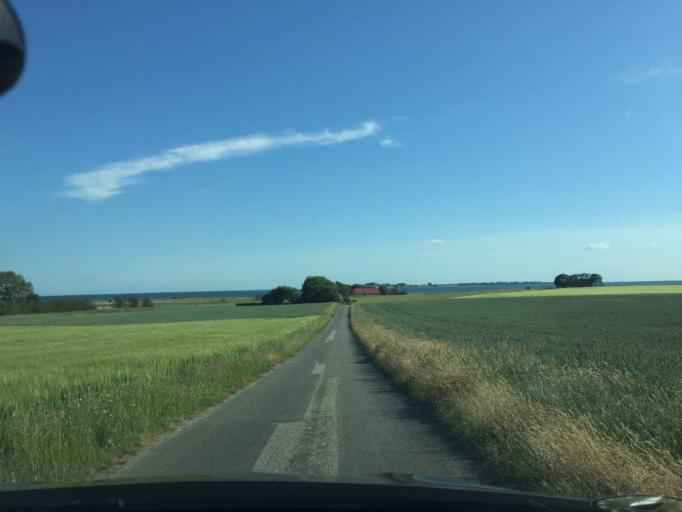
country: DK
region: Zealand
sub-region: Slagelse Kommune
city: Skaelskor
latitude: 55.2013
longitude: 11.1873
